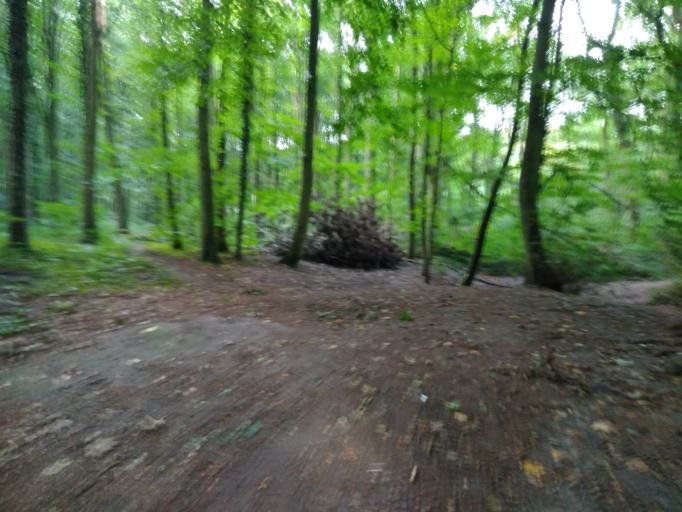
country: DE
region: North Rhine-Westphalia
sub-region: Regierungsbezirk Munster
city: Gladbeck
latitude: 51.6021
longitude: 6.9777
